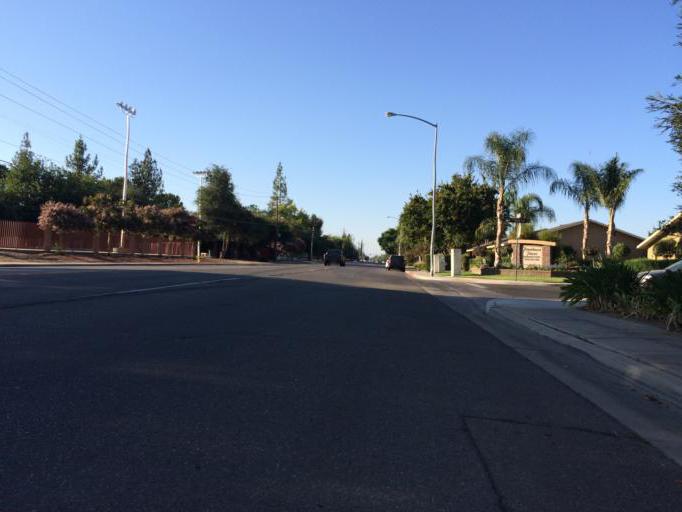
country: US
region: California
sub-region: Fresno County
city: Clovis
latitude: 36.8185
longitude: -119.7134
